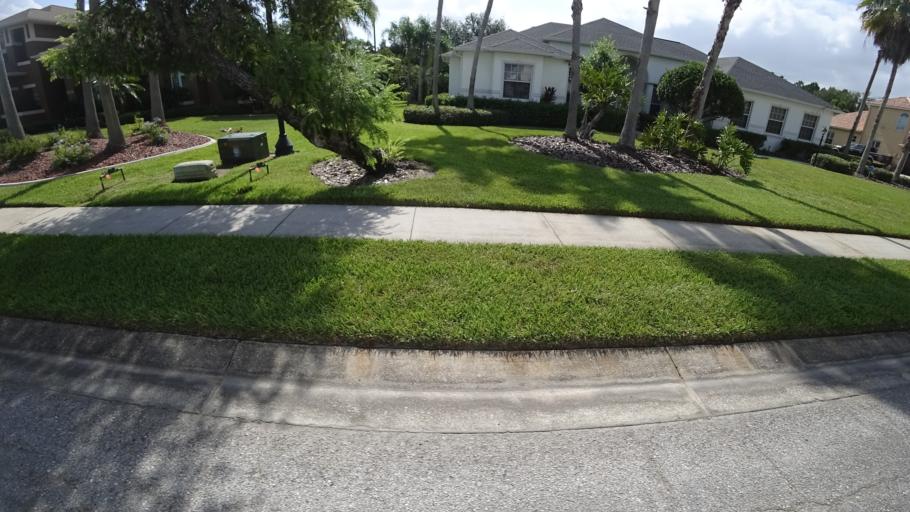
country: US
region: Florida
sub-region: Sarasota County
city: The Meadows
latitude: 27.4045
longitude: -82.4332
